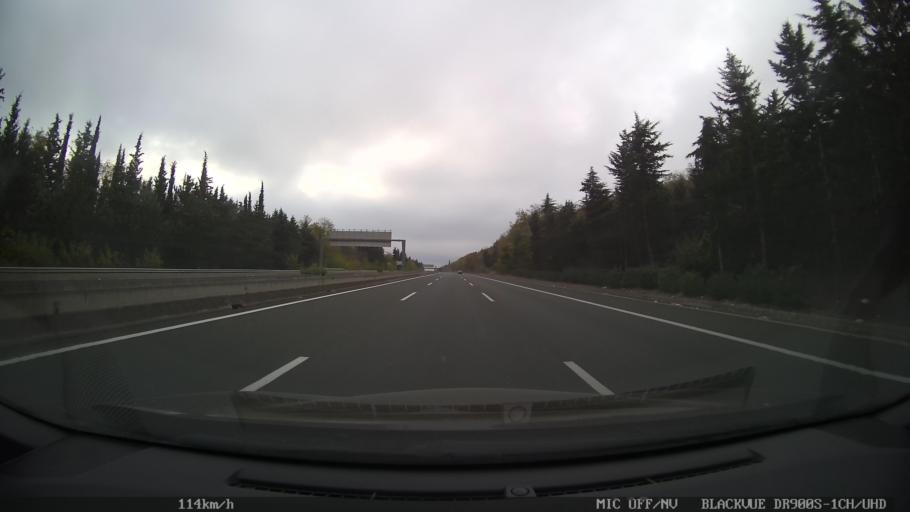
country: GR
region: Central Macedonia
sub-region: Nomos Pierias
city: Makrygialos
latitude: 40.4518
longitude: 22.5802
